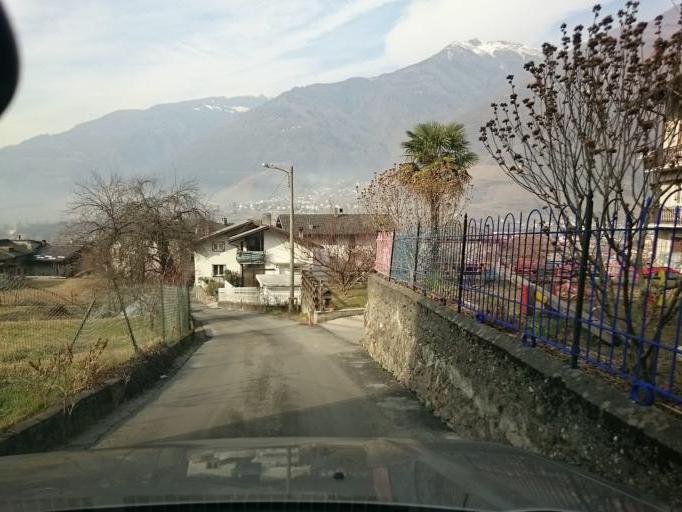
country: IT
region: Lombardy
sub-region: Provincia di Sondrio
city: Villa
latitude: 46.1849
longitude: 10.1334
